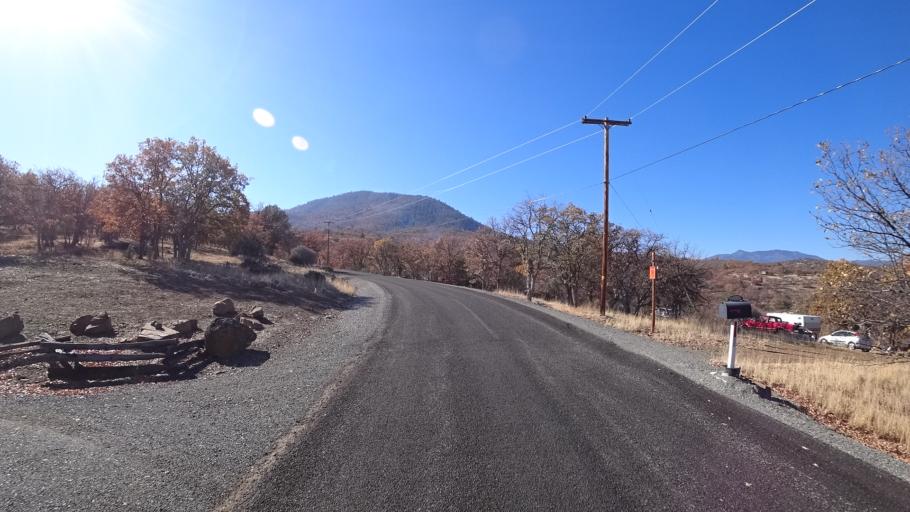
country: US
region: California
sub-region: Siskiyou County
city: Montague
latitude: 41.8825
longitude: -122.4895
